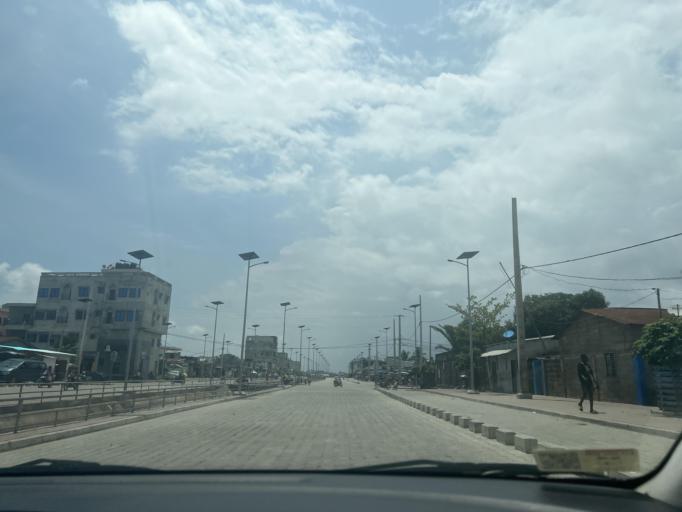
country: BJ
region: Littoral
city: Cotonou
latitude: 6.3887
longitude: 2.4414
